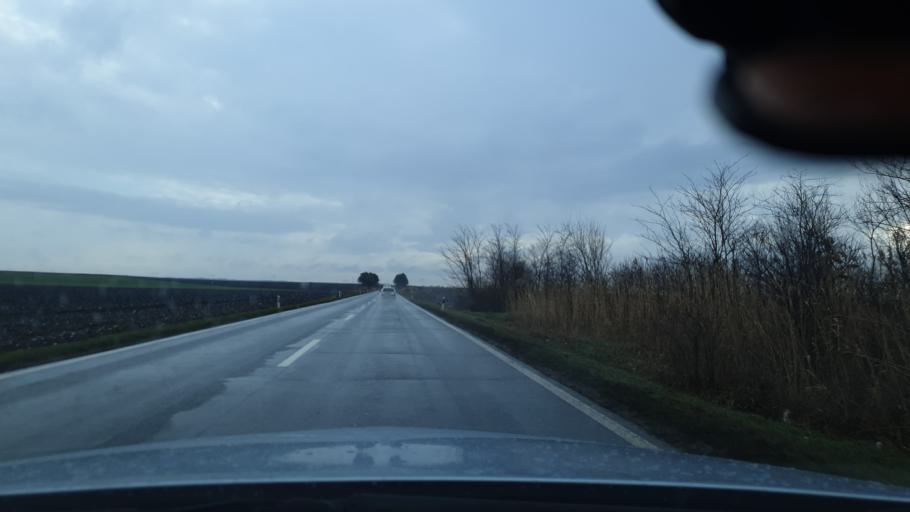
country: RS
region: Autonomna Pokrajina Vojvodina
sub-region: Juznobanatski Okrug
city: Kovin
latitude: 44.8331
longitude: 20.8238
